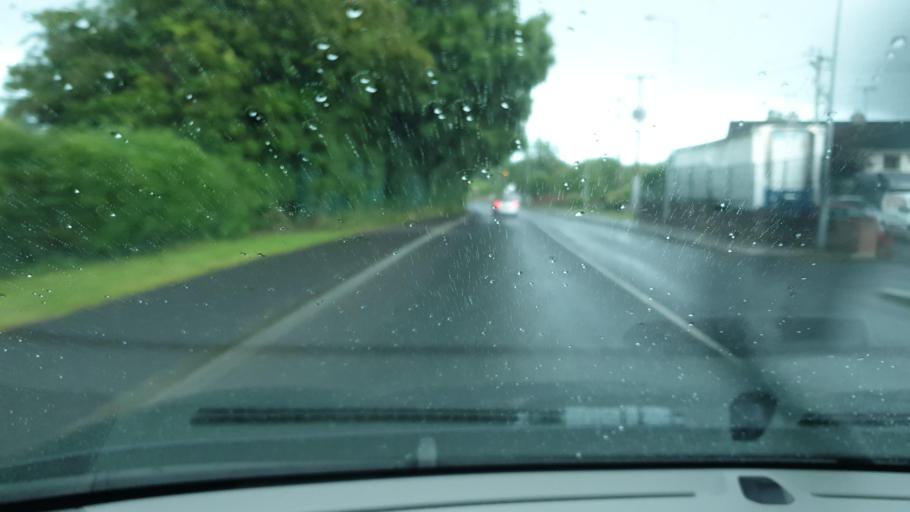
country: IE
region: Leinster
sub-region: An Mhi
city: Navan
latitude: 53.6452
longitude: -6.6914
